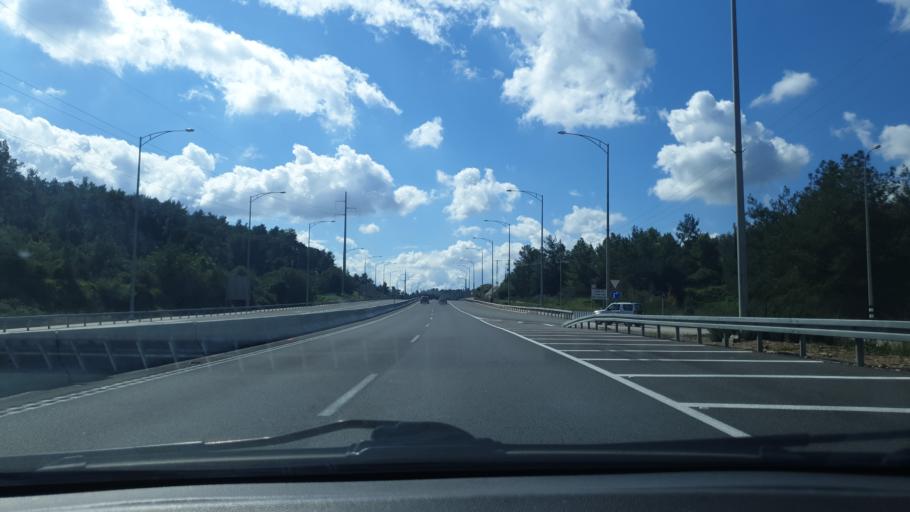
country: IL
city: Mevo horon
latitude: 31.8079
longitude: 35.0183
